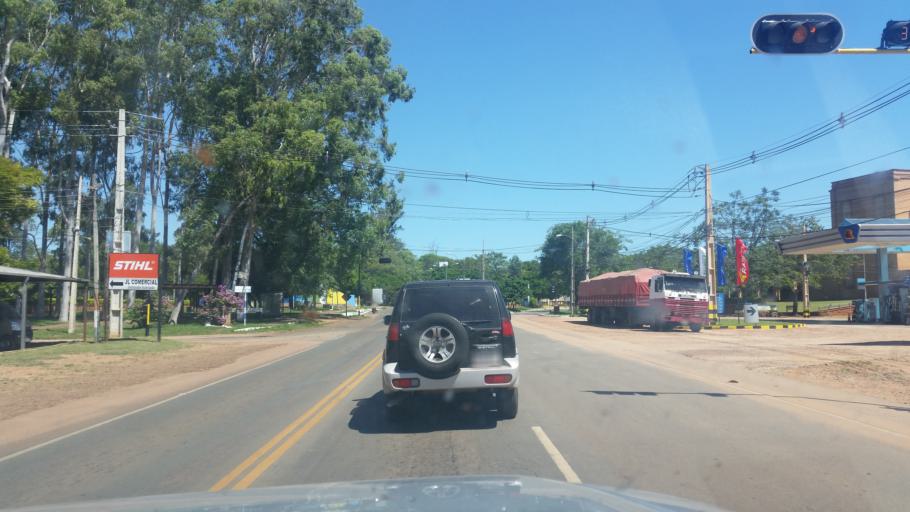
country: PY
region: Misiones
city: San Juan Bautista
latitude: -26.6662
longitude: -57.1331
